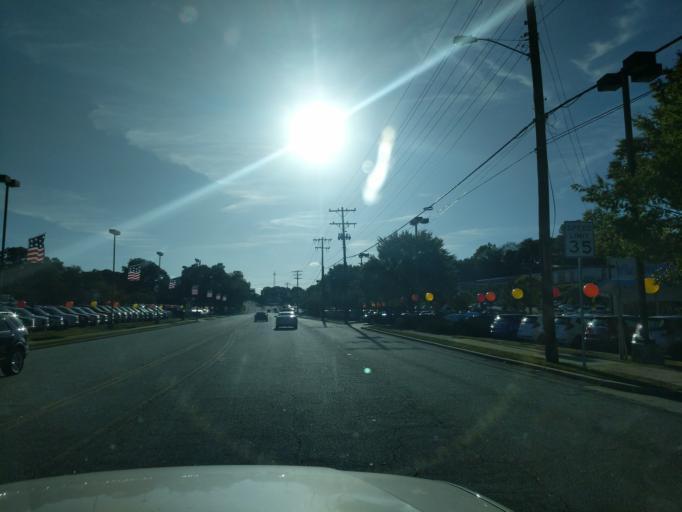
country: US
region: South Carolina
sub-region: Spartanburg County
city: Spartanburg
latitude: 34.9590
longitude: -81.9250
